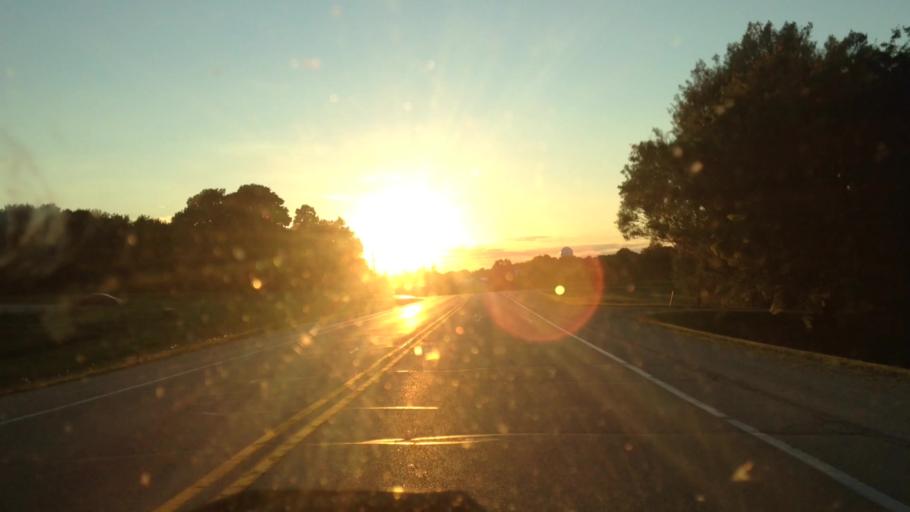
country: US
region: Wisconsin
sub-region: Dodge County
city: Theresa
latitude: 43.4385
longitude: -88.4782
